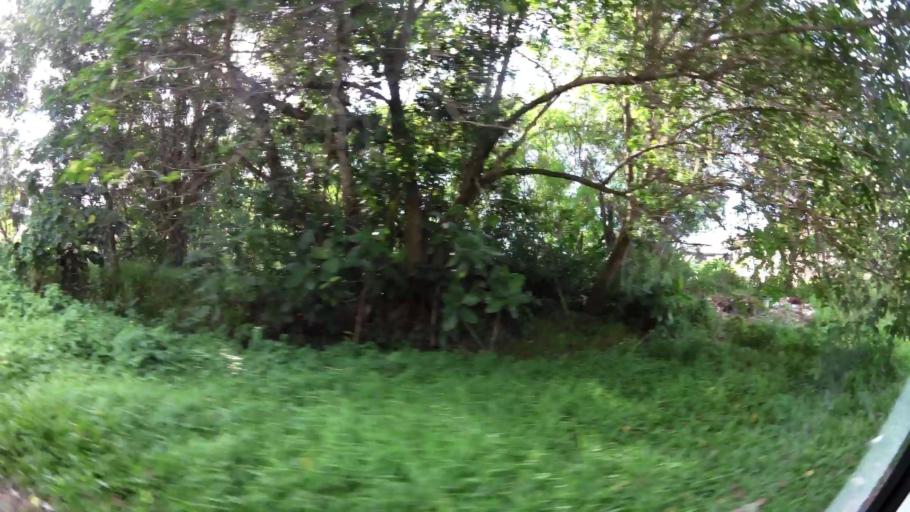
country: BN
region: Brunei and Muara
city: Bandar Seri Begawan
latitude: 4.9832
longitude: 114.9679
